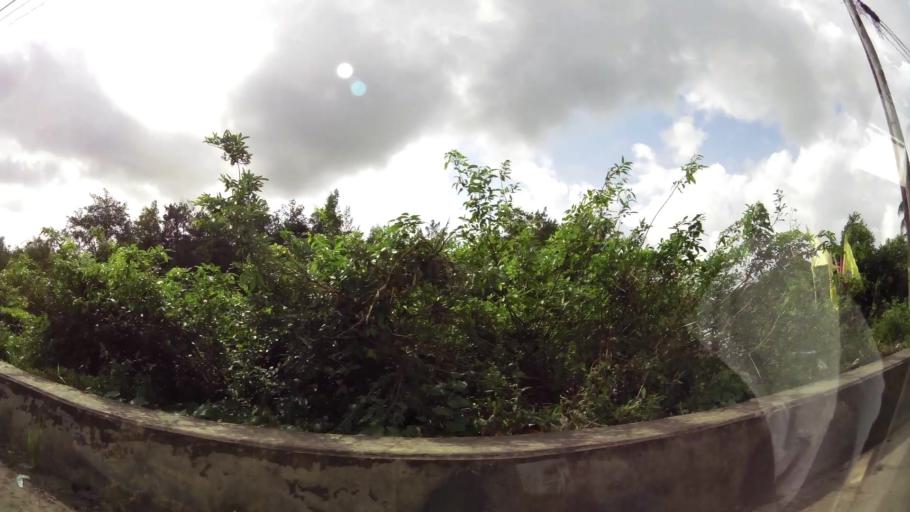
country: GY
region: Demerara-Mahaica
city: Mahaica Village
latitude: 6.6681
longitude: -57.9252
